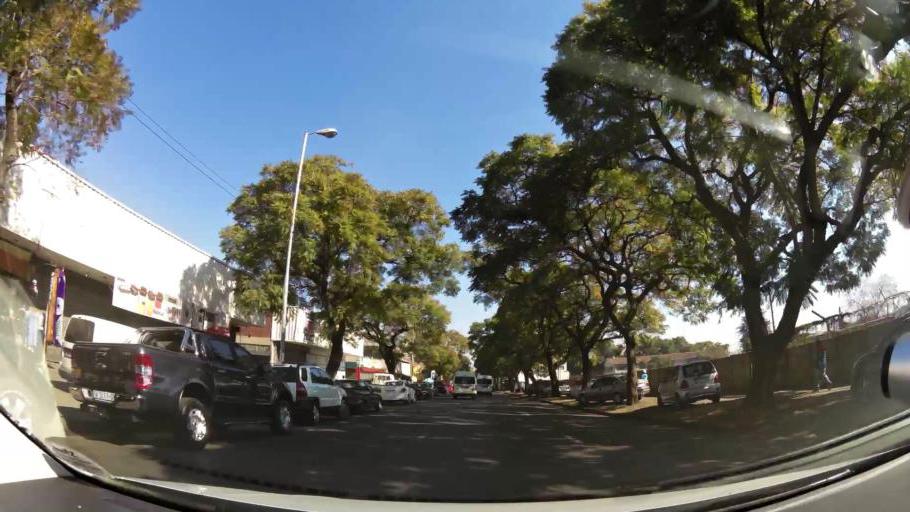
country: ZA
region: Gauteng
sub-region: City of Tshwane Metropolitan Municipality
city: Pretoria
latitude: -25.7407
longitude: 28.1842
